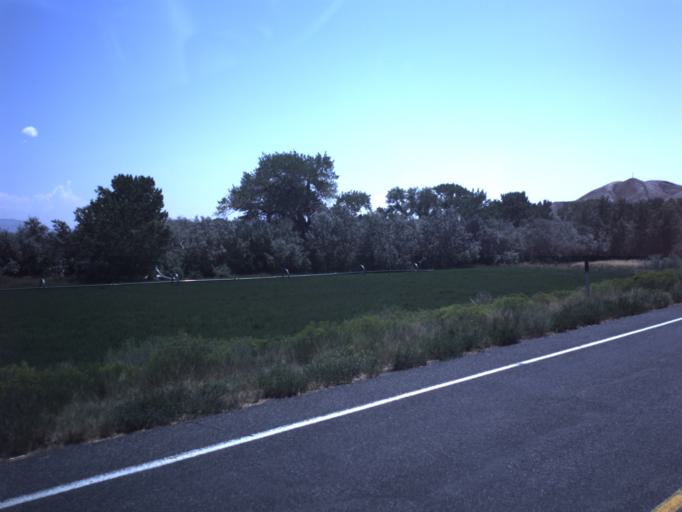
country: US
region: Utah
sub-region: Emery County
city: Orangeville
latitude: 39.2193
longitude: -111.0681
